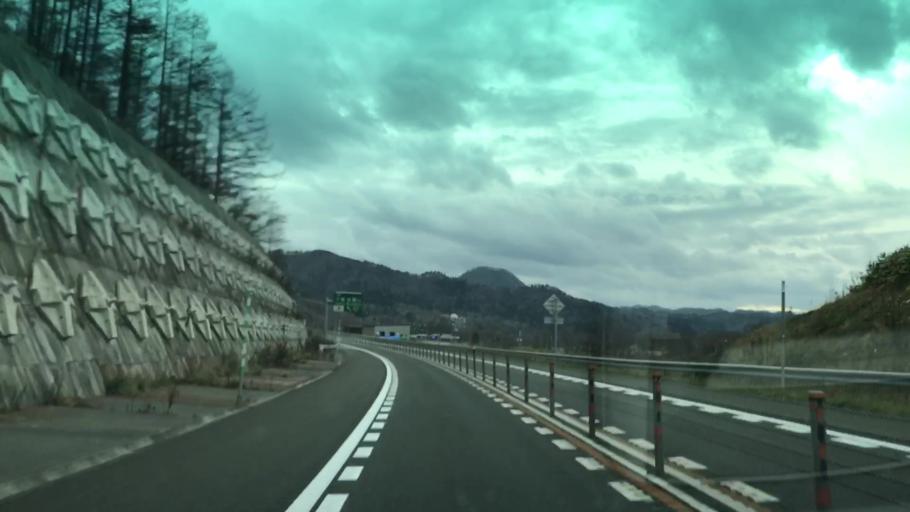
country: JP
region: Hokkaido
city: Iwamizawa
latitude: 42.9276
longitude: 142.0362
